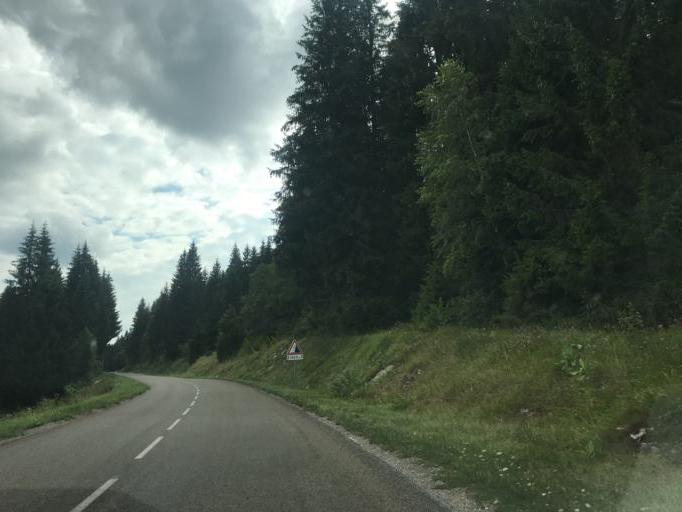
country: FR
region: Franche-Comte
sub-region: Departement du Jura
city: Valfin-les-Saint-Claude
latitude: 46.4974
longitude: 5.8536
